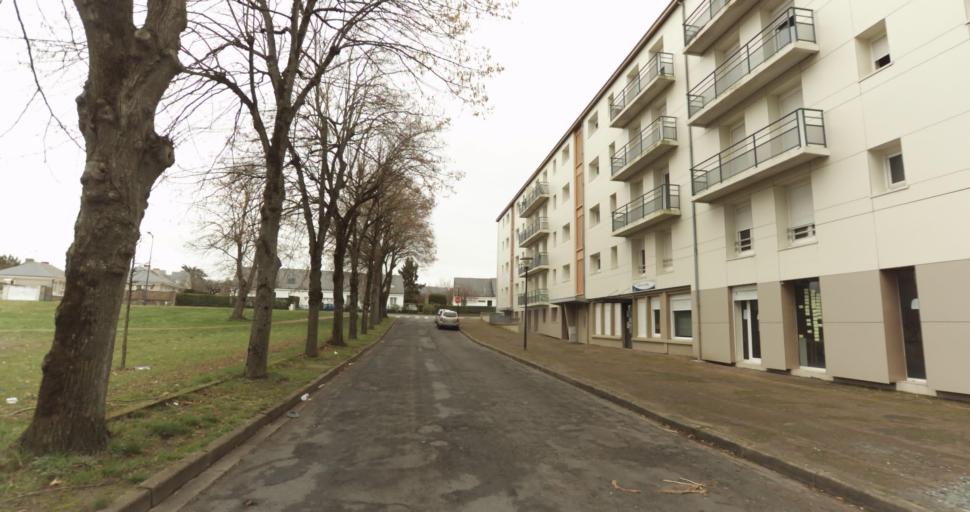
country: FR
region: Pays de la Loire
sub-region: Departement de Maine-et-Loire
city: Saumur
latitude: 47.2506
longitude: -0.0674
